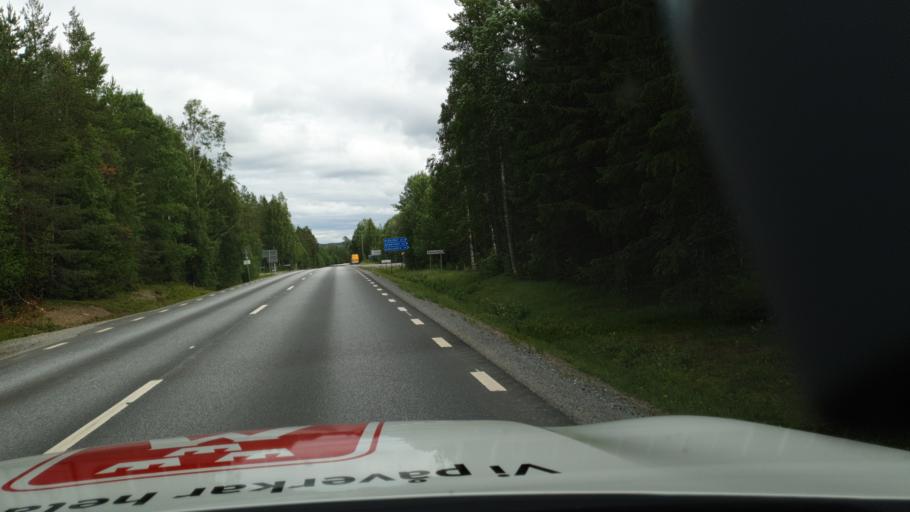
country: SE
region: Vaesterbotten
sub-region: Bjurholms Kommun
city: Bjurholm
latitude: 63.9243
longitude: 19.0955
